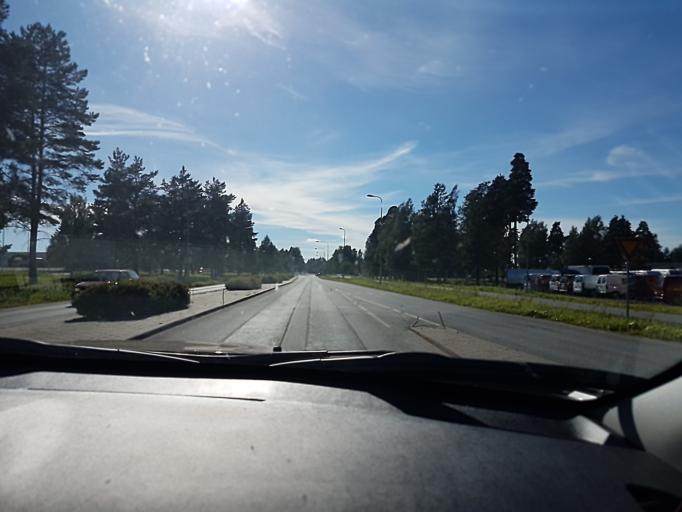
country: FI
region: Southern Ostrobothnia
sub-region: Seinaejoki
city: Seinaejoki
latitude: 62.7926
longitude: 22.8748
